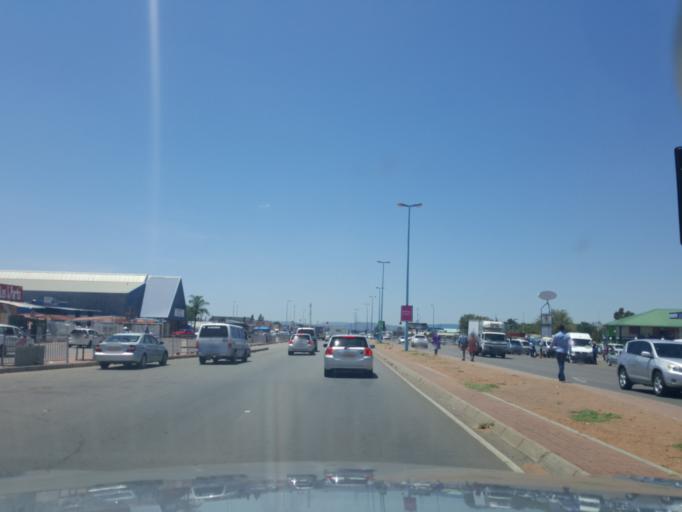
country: BW
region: Kweneng
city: Mogoditshane
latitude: -24.6174
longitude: 25.8645
